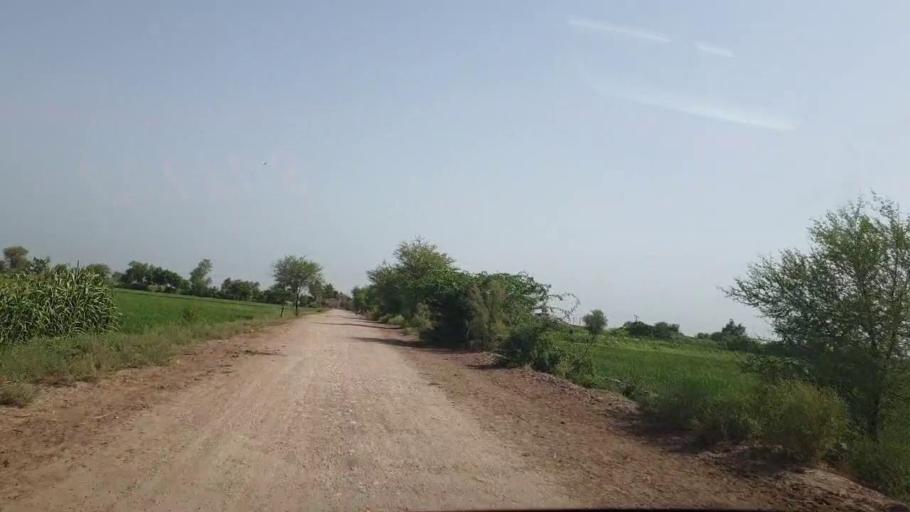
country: PK
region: Sindh
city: Sakrand
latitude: 26.2898
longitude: 68.2265
